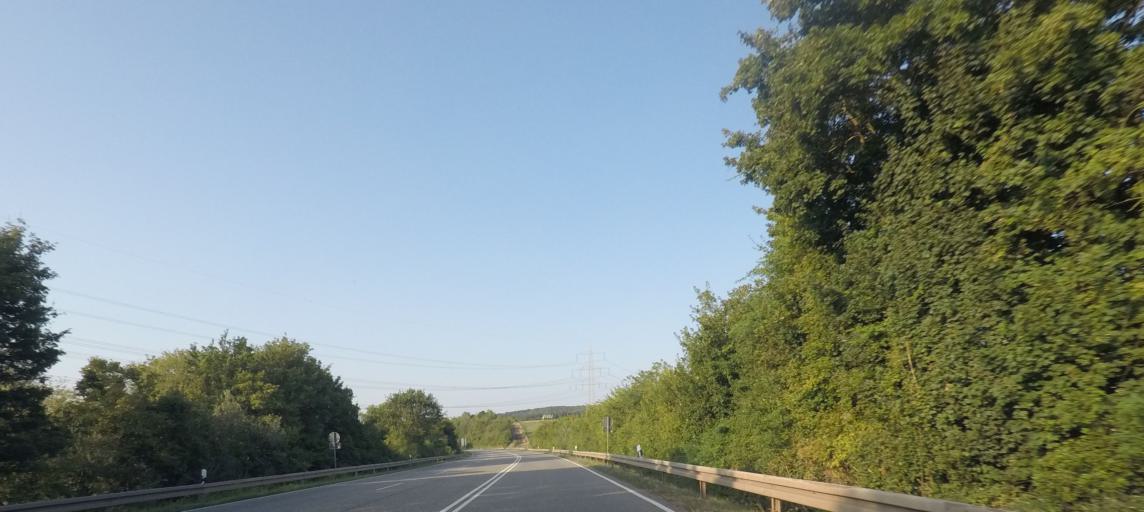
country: DE
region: Saarland
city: Heusweiler
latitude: 49.3720
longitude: 6.9263
